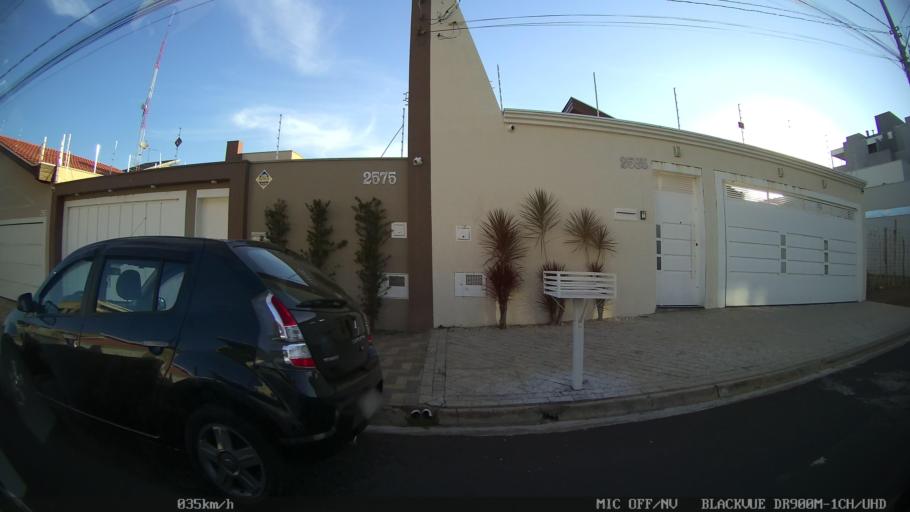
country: BR
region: Sao Paulo
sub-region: Franca
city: Franca
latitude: -20.5090
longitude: -47.3962
